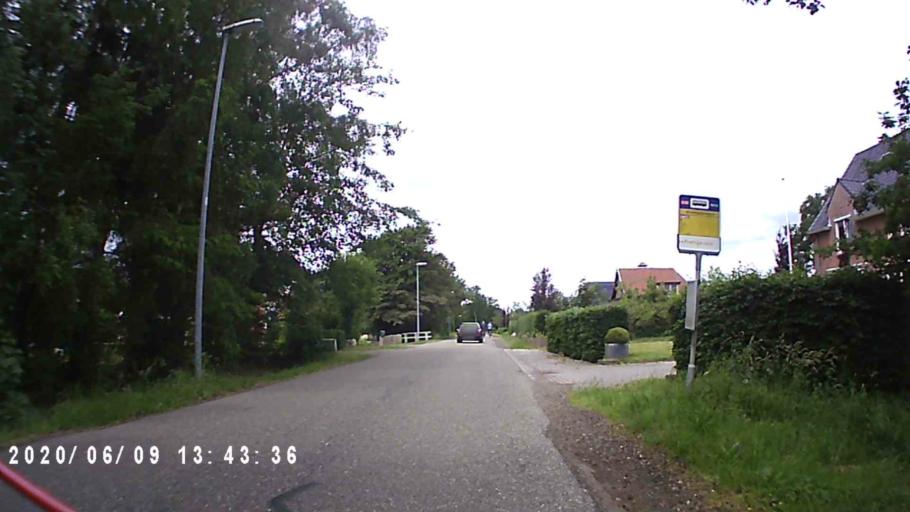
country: NL
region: Groningen
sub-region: Gemeente Haren
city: Haren
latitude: 53.2173
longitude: 6.6407
